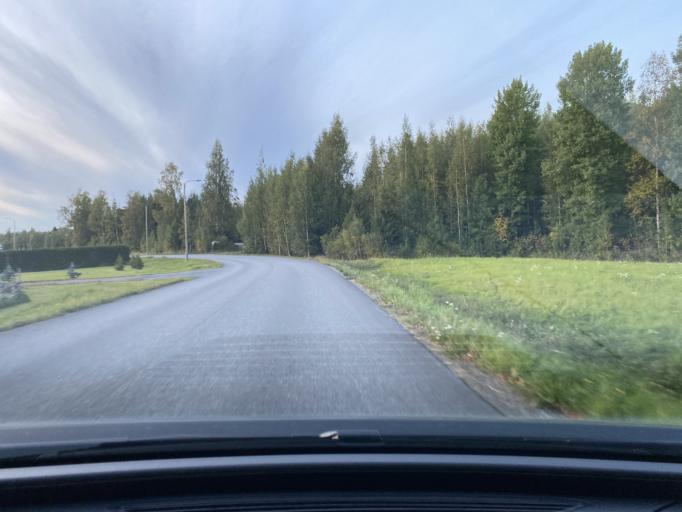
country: FI
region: Satakunta
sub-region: Pori
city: Huittinen
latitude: 61.1714
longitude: 22.7153
